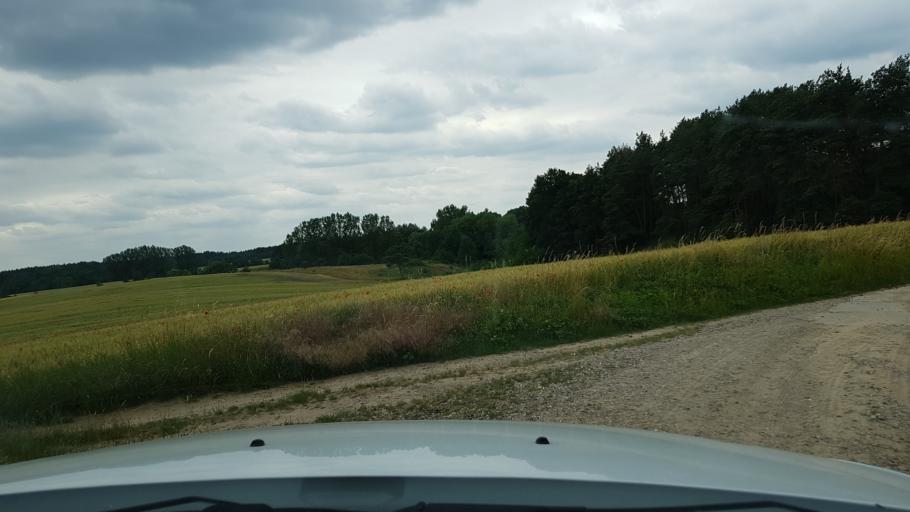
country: PL
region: West Pomeranian Voivodeship
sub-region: Powiat mysliborski
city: Boleszkowice
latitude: 52.6768
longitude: 14.6240
